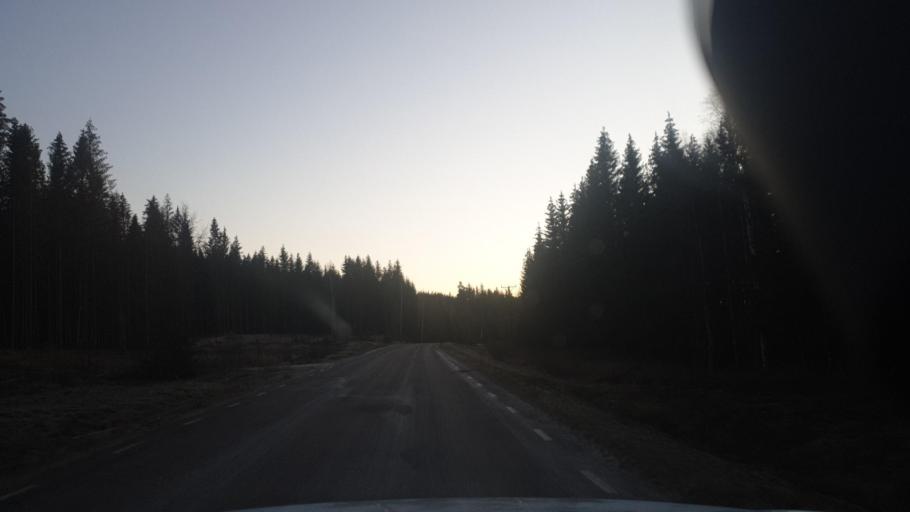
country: SE
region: Vaermland
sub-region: Eda Kommun
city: Charlottenberg
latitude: 59.9436
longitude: 12.3844
